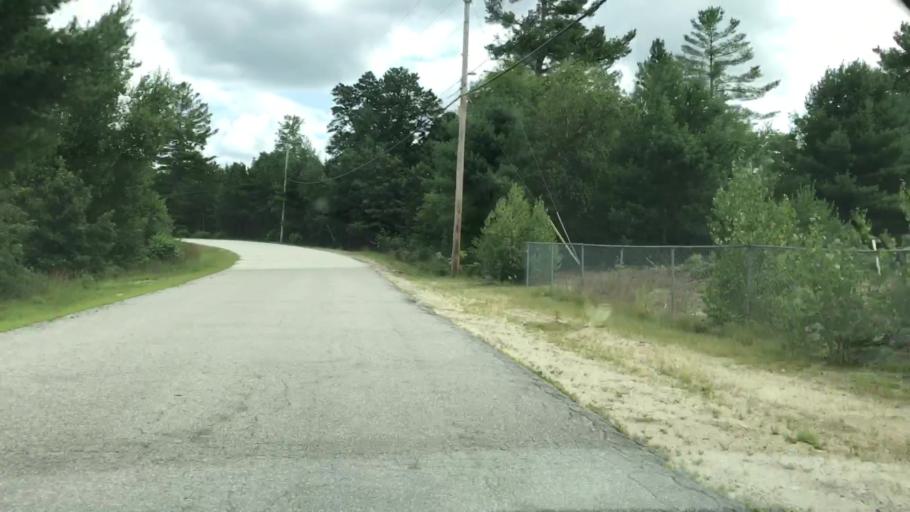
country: US
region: New Hampshire
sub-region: Hillsborough County
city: Hollis
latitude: 42.8060
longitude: -71.5847
